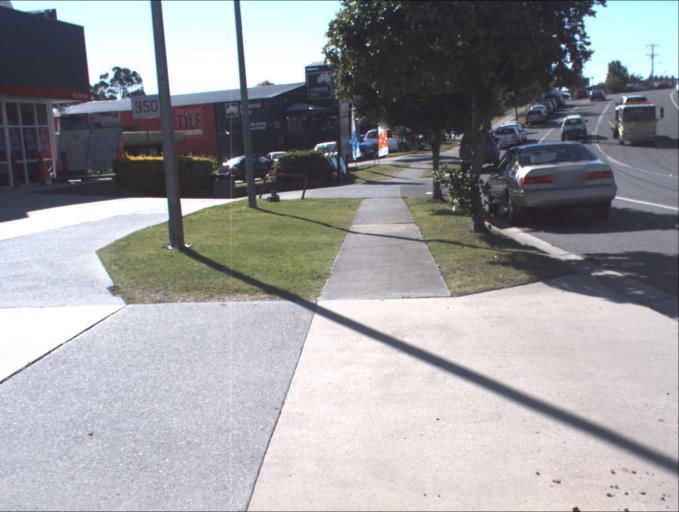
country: AU
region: Queensland
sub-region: Logan
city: Slacks Creek
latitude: -27.6348
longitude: 153.1327
